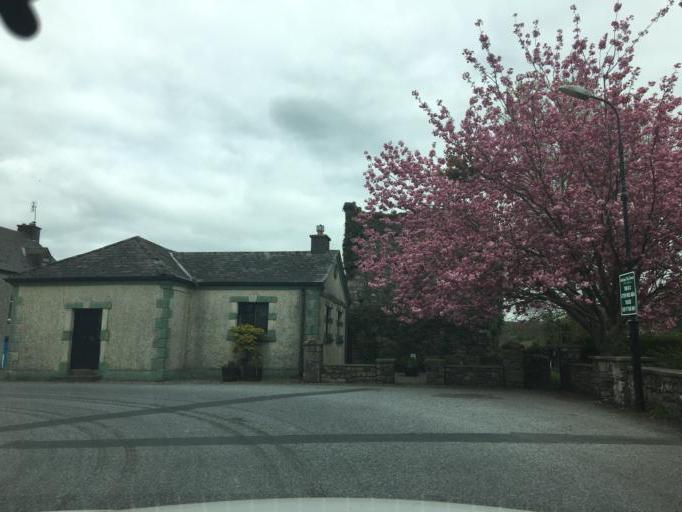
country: IE
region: Leinster
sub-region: Kilkenny
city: Thomastown
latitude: 52.4880
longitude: -7.0640
